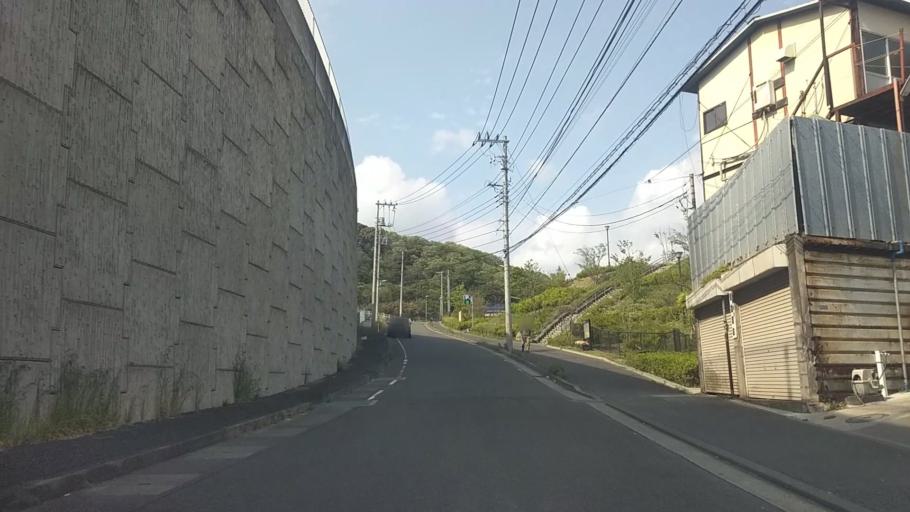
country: JP
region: Kanagawa
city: Kamakura
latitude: 35.3819
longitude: 139.5535
